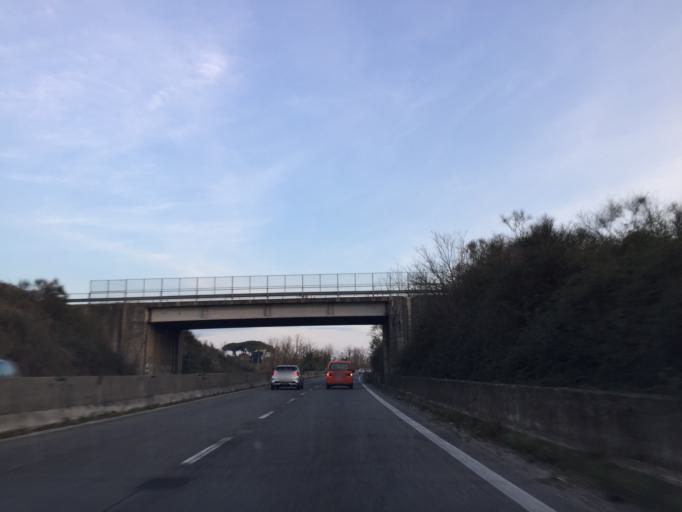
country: IT
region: Latium
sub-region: Citta metropolitana di Roma Capitale
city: Formello
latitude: 42.0325
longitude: 12.4289
